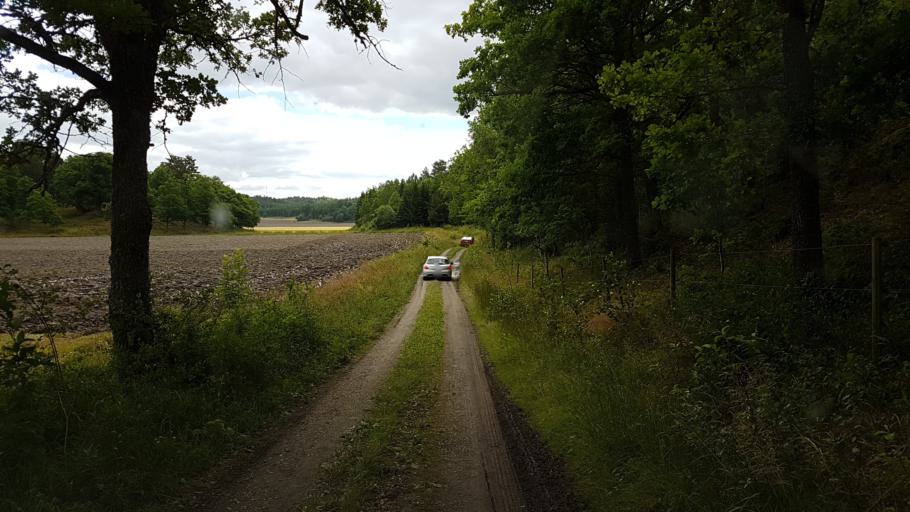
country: SE
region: OEstergoetland
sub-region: Valdemarsviks Kommun
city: Gusum
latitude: 58.4301
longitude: 16.5752
